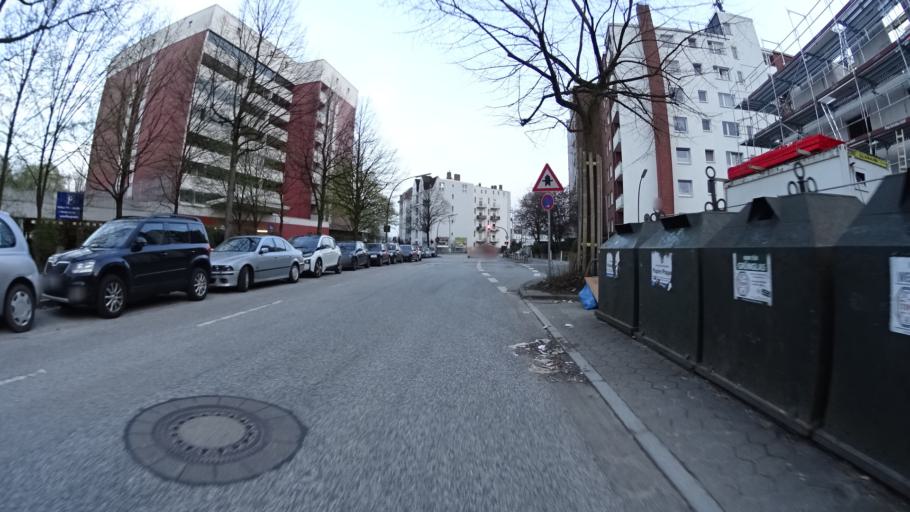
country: DE
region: Hamburg
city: Hamburg-Nord
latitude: 53.5869
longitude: 9.9671
